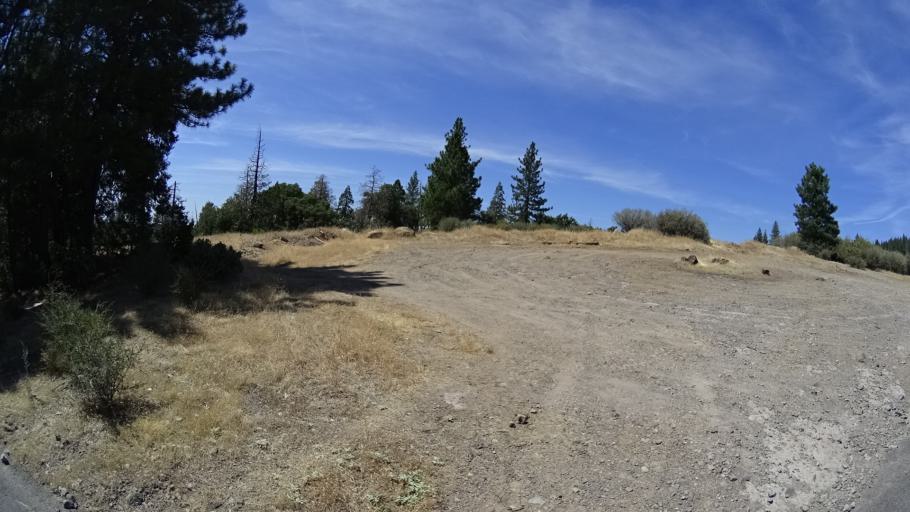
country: US
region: California
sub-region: Calaveras County
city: Forest Meadows
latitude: 38.1968
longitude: -120.3999
